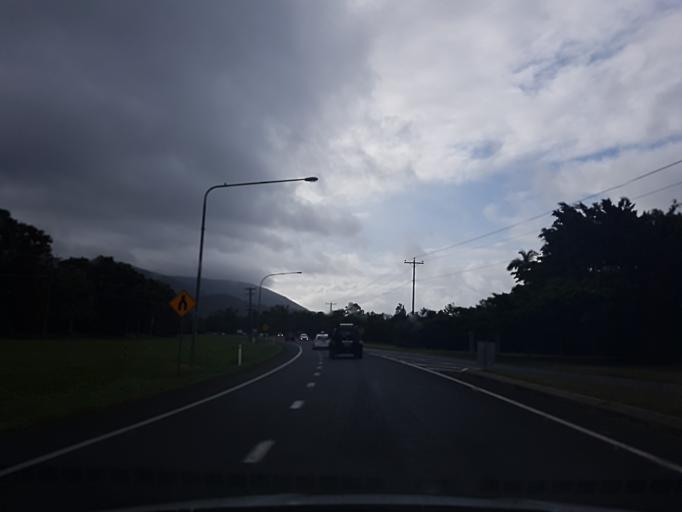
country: AU
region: Queensland
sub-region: Cairns
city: Trinity Beach
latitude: -16.7910
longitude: 145.6777
